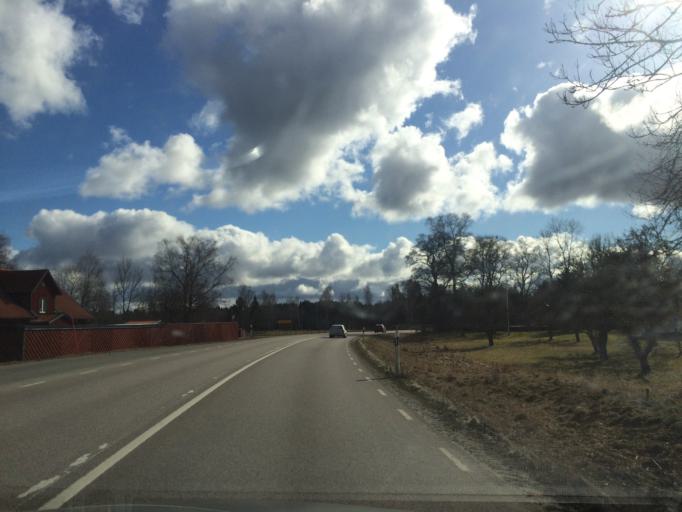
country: SE
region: Vaestra Goetaland
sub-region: Skara Kommun
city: Skara
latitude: 58.3292
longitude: 13.4365
